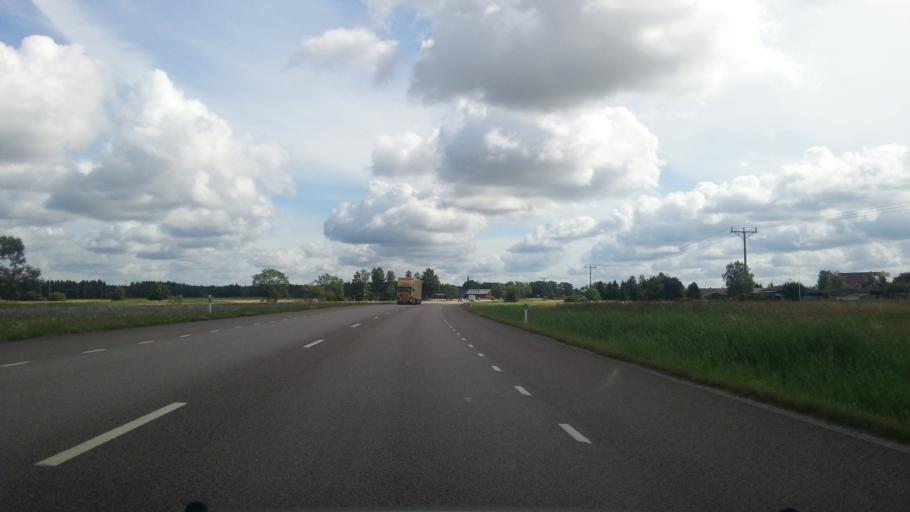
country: SE
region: Vaestra Goetaland
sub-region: Gotene Kommun
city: Goetene
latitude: 58.5313
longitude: 13.4684
